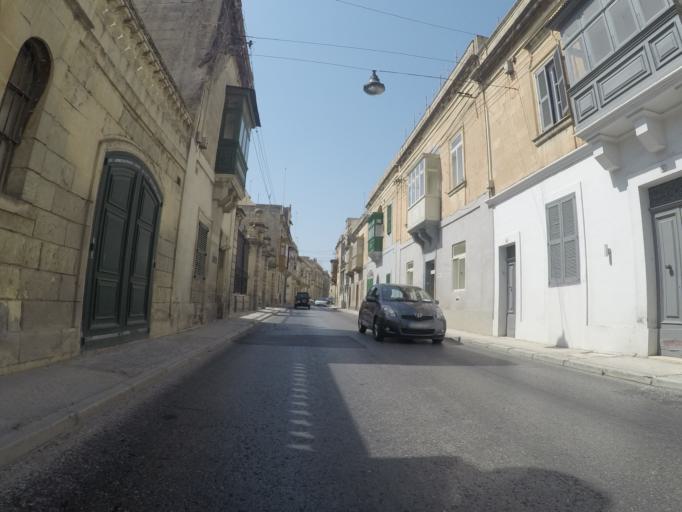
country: MT
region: Ir-Rabat
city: Rabat
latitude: 35.8795
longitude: 14.4008
